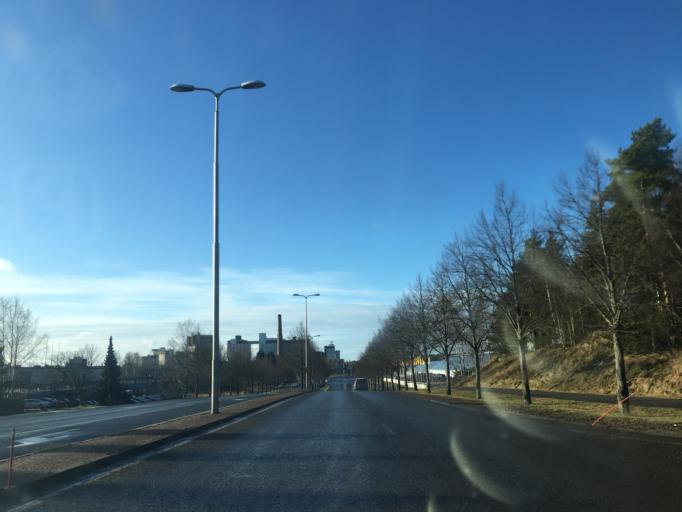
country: FI
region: Varsinais-Suomi
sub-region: Turku
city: Raisio
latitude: 60.4862
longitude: 22.1484
